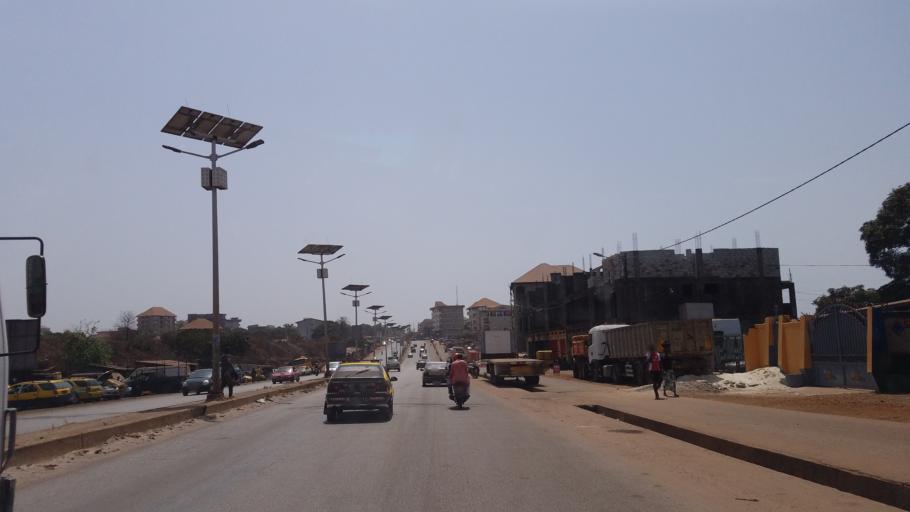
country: GN
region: Conakry
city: Conakry
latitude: 9.6505
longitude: -13.5818
